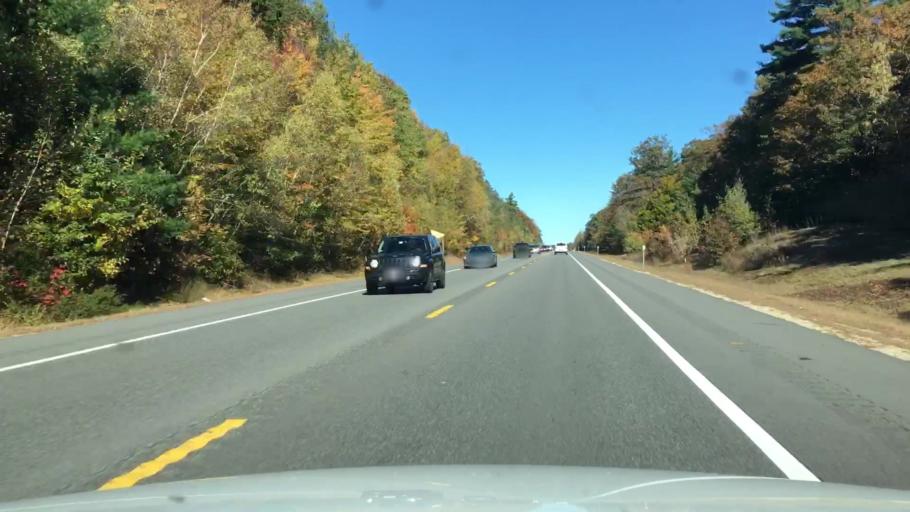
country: US
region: New Hampshire
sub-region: Strafford County
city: Rochester
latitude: 43.3612
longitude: -70.9870
